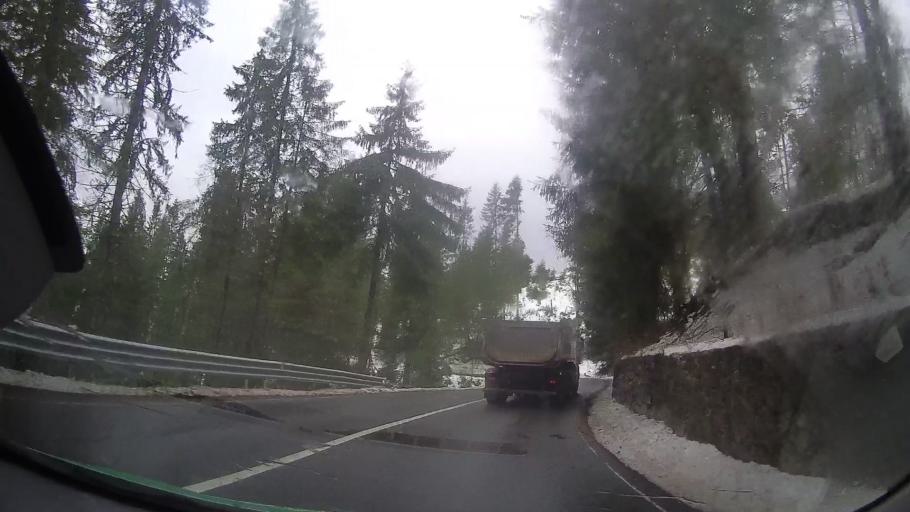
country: RO
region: Harghita
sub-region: Municipiul Gheorgheni
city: Gheorgheni
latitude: 46.7793
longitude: 25.7280
